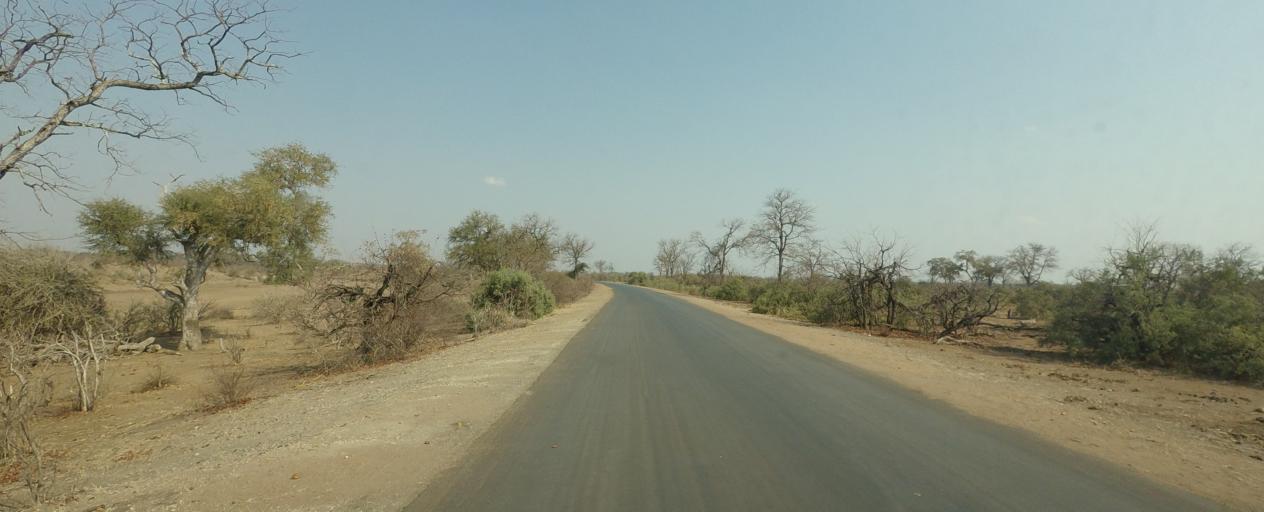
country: ZA
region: Limpopo
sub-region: Mopani District Municipality
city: Giyani
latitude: -23.1023
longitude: 31.4274
